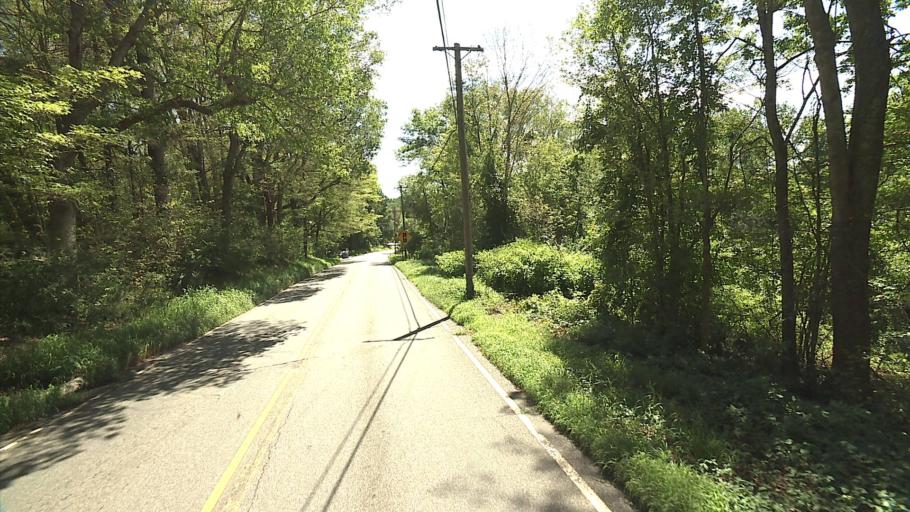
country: US
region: Connecticut
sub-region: Windham County
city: South Woodstock
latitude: 41.8624
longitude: -72.0066
